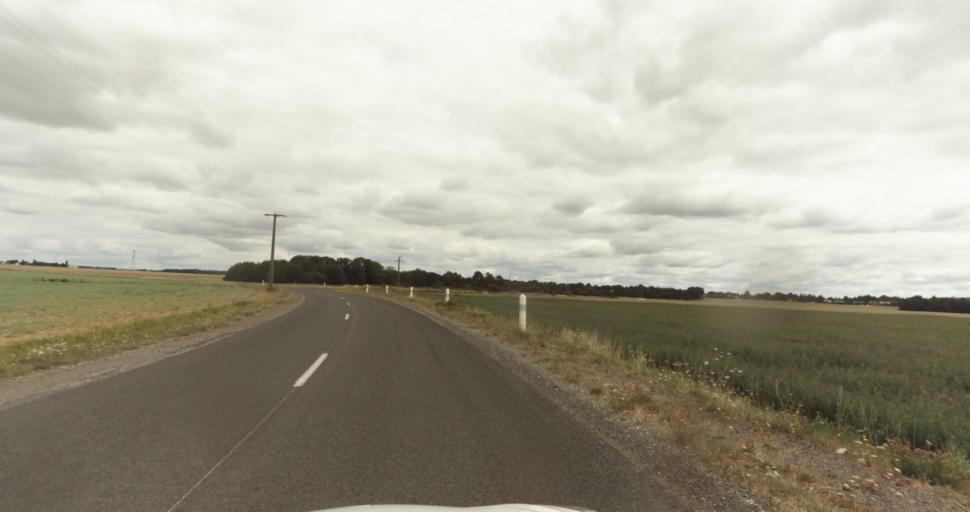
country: FR
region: Haute-Normandie
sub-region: Departement de l'Eure
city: La Madeleine-de-Nonancourt
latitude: 48.8339
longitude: 1.2295
